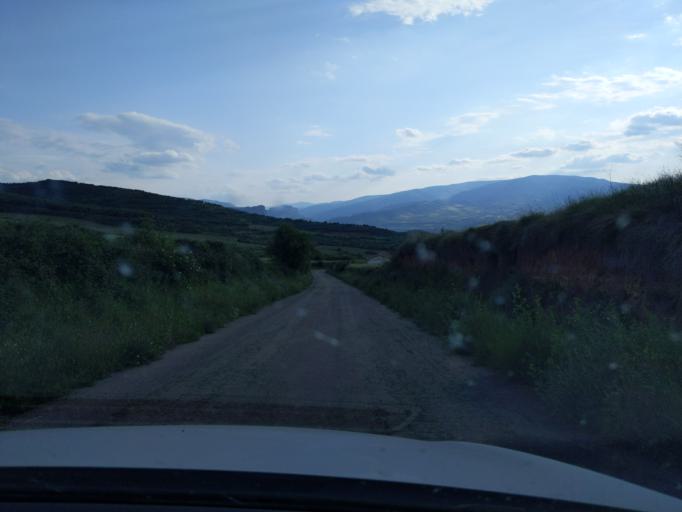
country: ES
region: La Rioja
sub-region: Provincia de La Rioja
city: Clavijo
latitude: 42.3537
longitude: -2.4479
